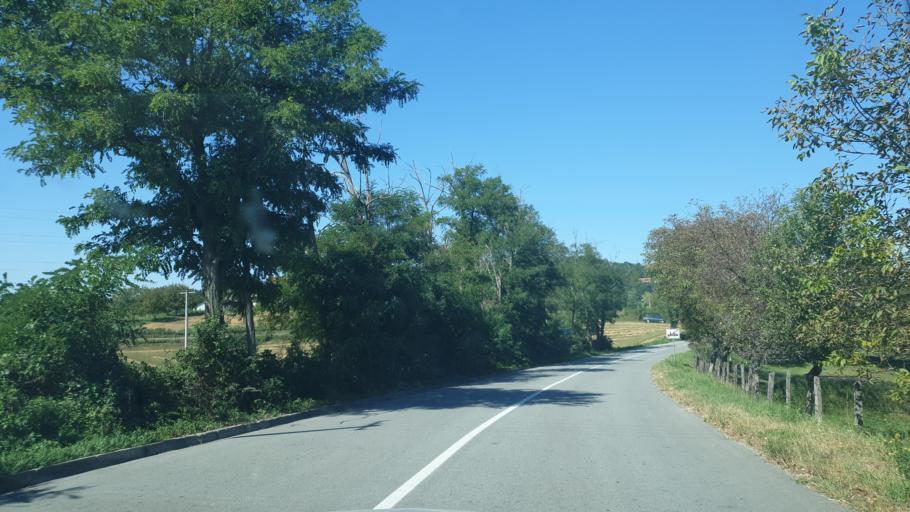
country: RS
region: Central Serbia
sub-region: Kolubarski Okrug
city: Mionica
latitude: 44.1916
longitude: 20.0281
